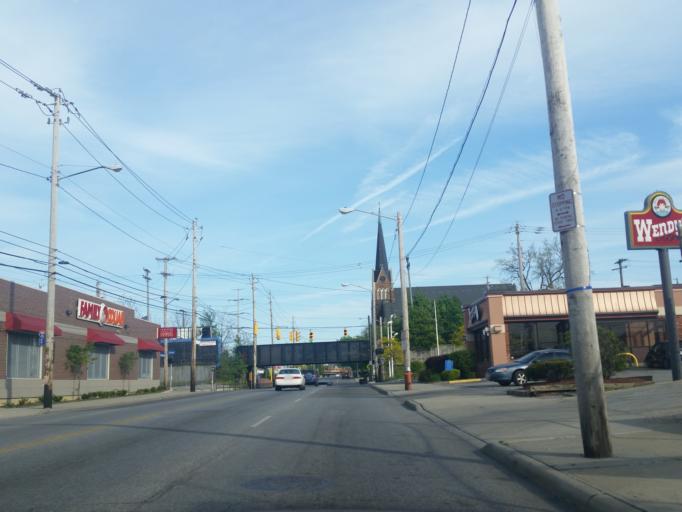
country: US
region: Ohio
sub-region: Cuyahoga County
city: Newburgh Heights
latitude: 41.4516
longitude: -81.6311
